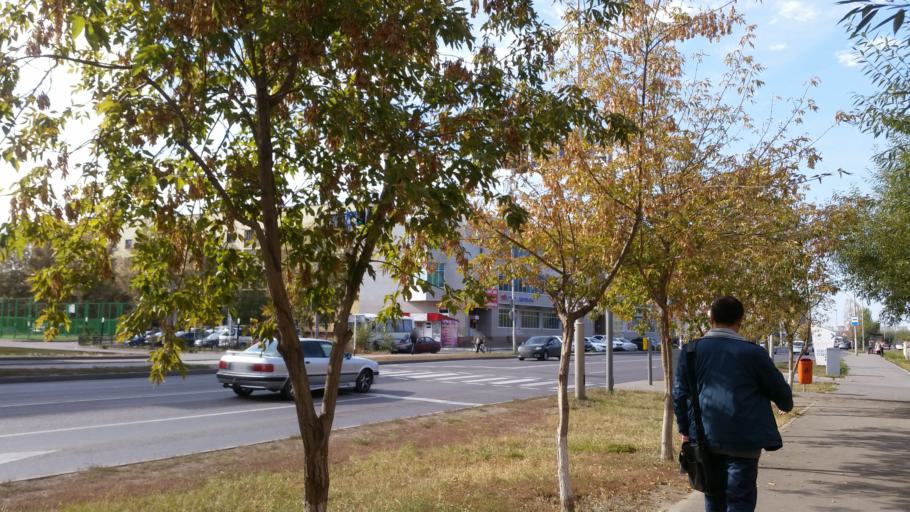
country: KZ
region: Astana Qalasy
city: Astana
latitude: 51.1610
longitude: 71.4877
